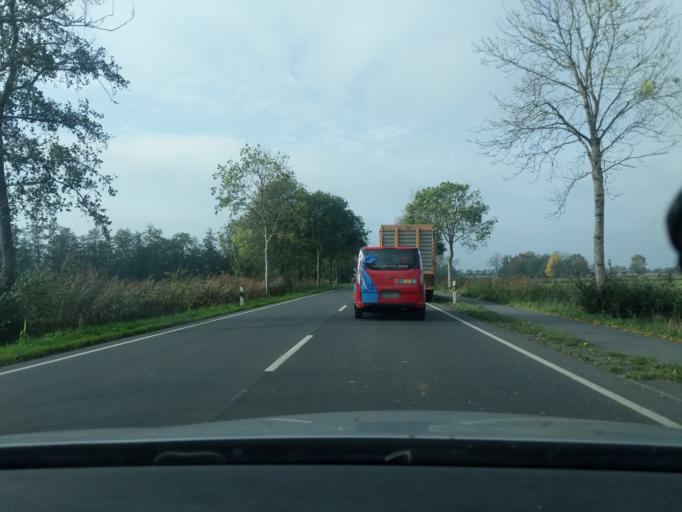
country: DE
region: Lower Saxony
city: Belum
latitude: 53.8181
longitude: 8.9843
